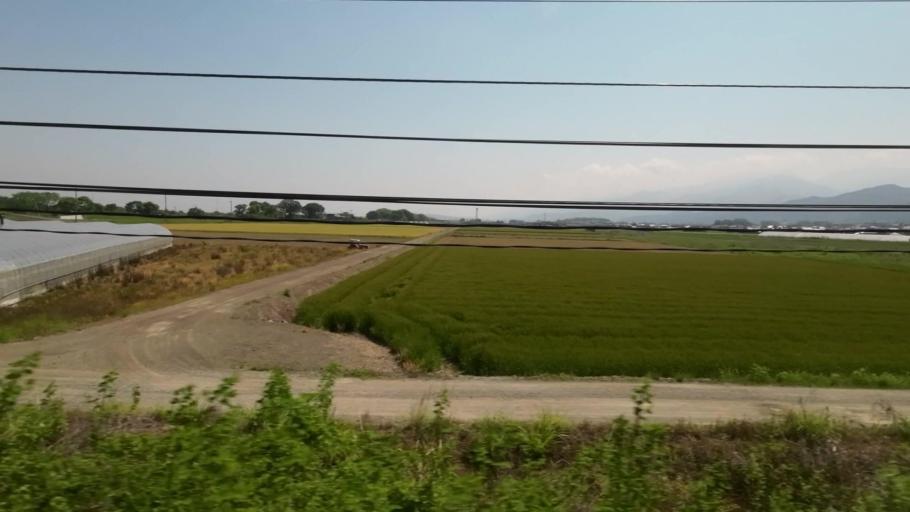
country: JP
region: Ehime
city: Saijo
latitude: 33.9028
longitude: 133.0995
